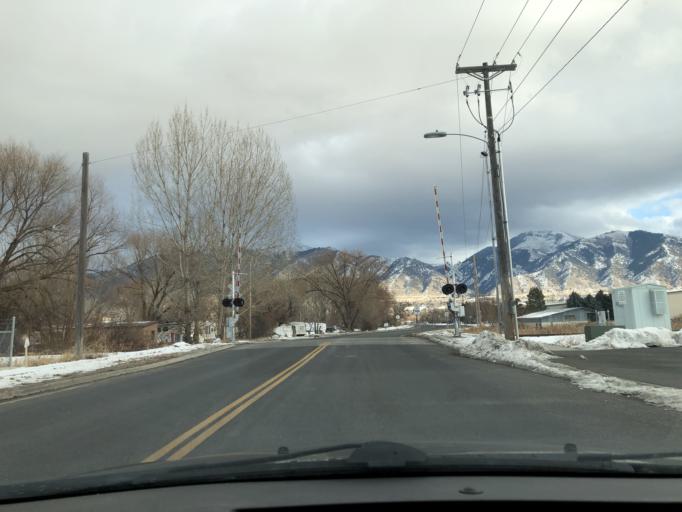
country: US
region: Utah
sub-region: Cache County
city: Providence
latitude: 41.7031
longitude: -111.8492
